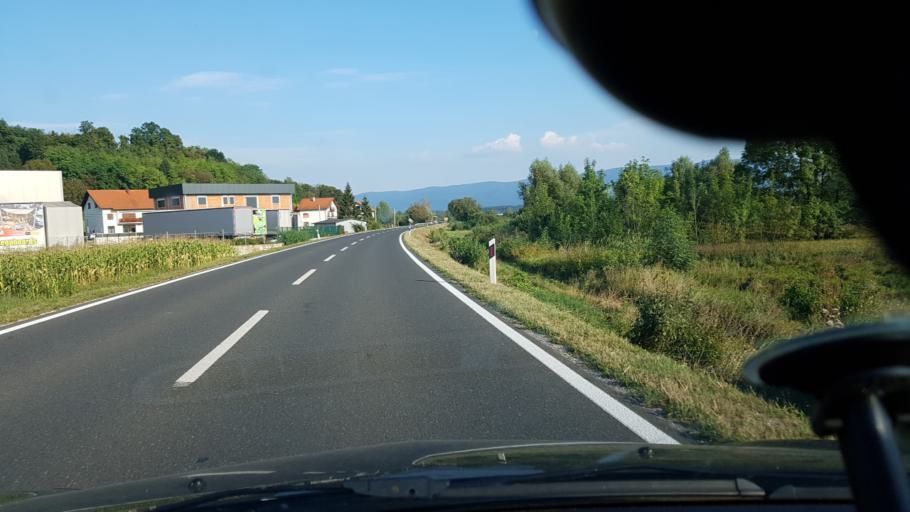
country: HR
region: Krapinsko-Zagorska
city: Zabok
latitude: 46.0178
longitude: 15.8647
